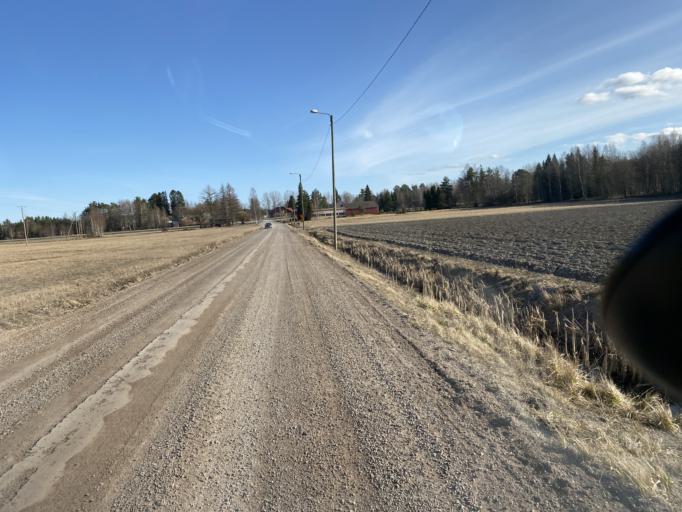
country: FI
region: Satakunta
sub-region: Rauma
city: Lappi
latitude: 61.1267
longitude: 21.9525
